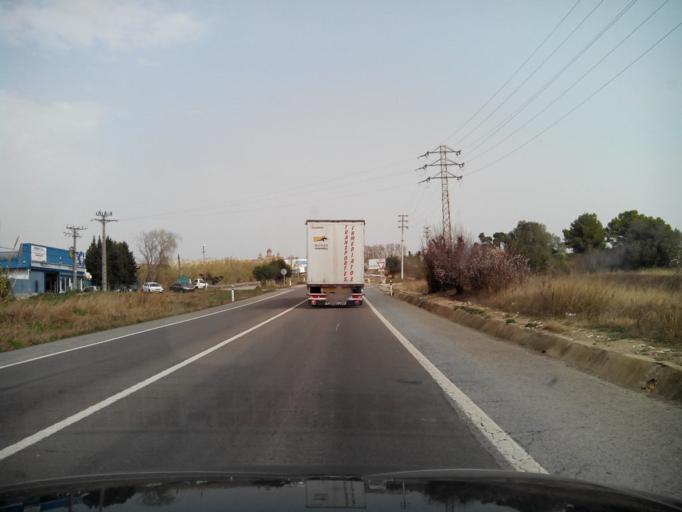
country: ES
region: Catalonia
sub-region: Provincia de Barcelona
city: Castellet
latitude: 41.2602
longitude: 1.5987
